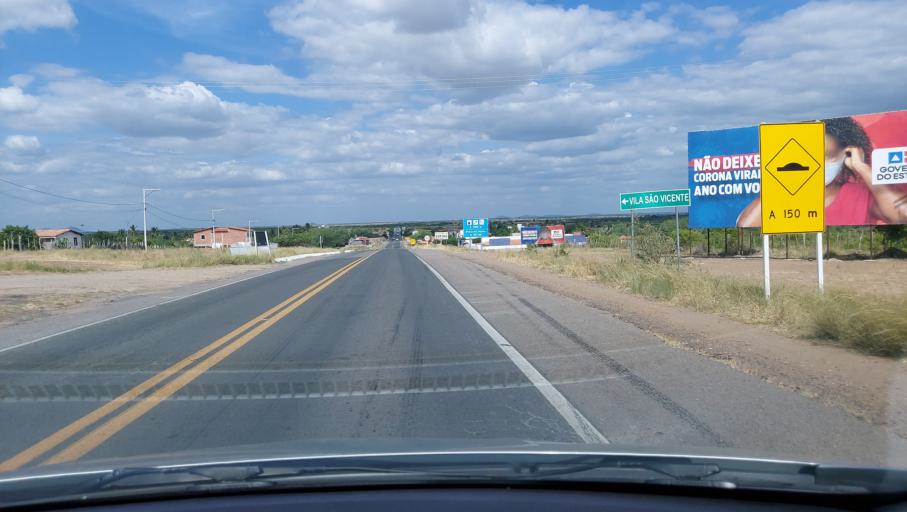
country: BR
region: Bahia
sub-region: Itaberaba
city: Itaberaba
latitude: -12.5180
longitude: -39.9428
